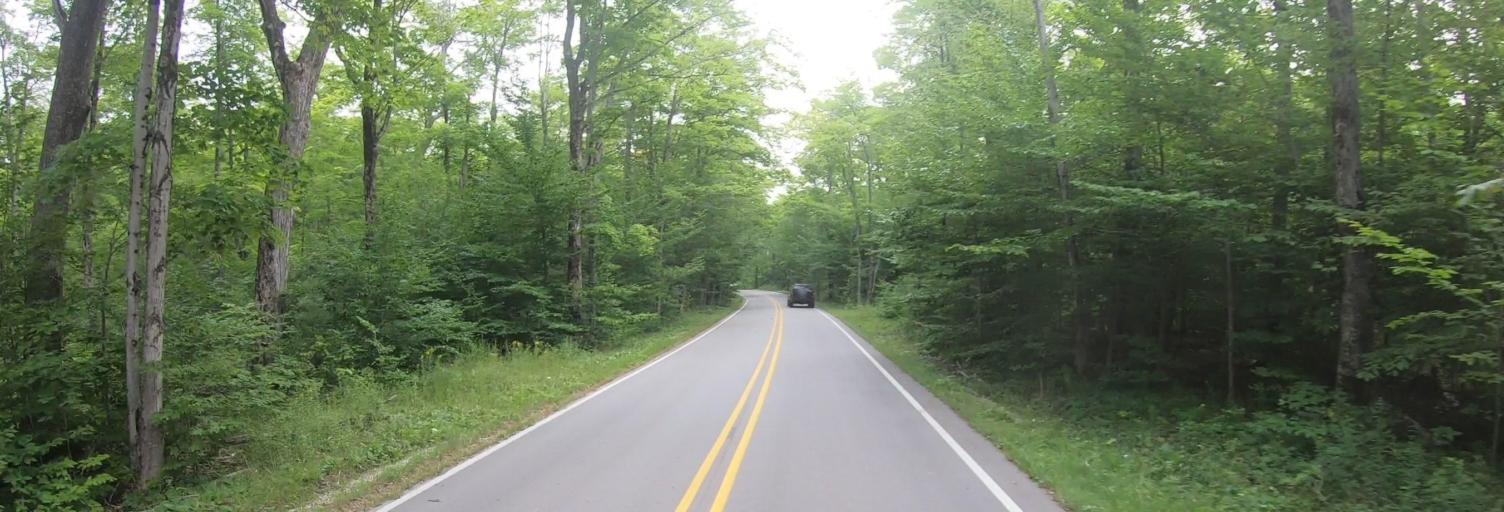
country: CA
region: Ontario
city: Thessalon
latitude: 45.9436
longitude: -83.5836
